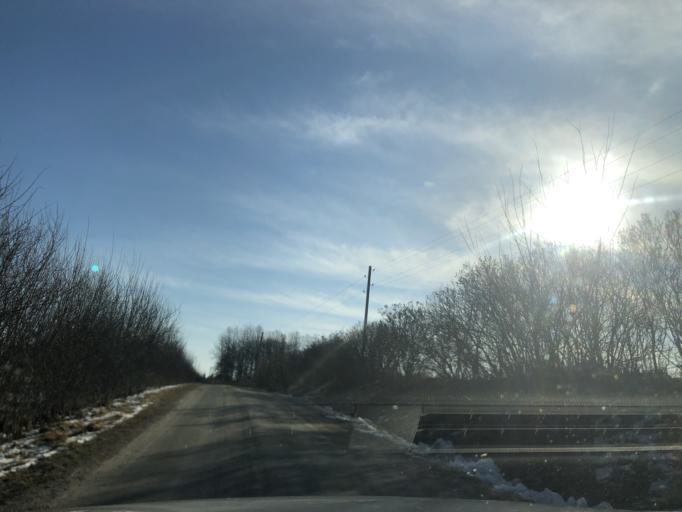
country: SE
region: Vaestra Goetaland
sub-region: Ulricehamns Kommun
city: Ulricehamn
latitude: 57.7964
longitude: 13.4478
